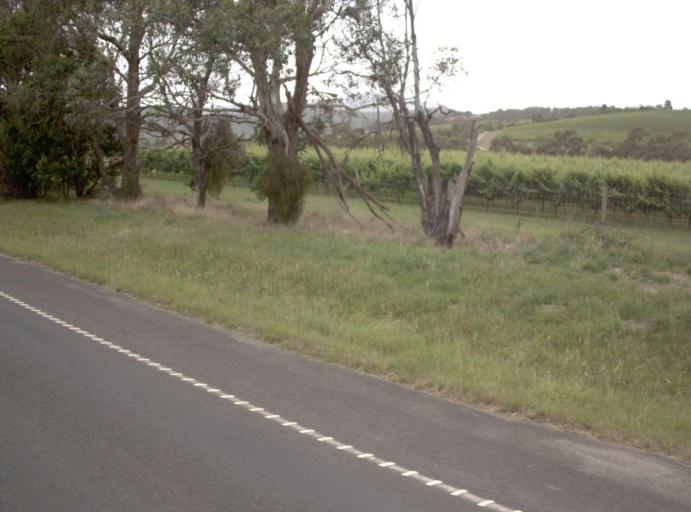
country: AU
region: Victoria
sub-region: Yarra Ranges
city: Yarra Glen
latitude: -37.6095
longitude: 145.4149
